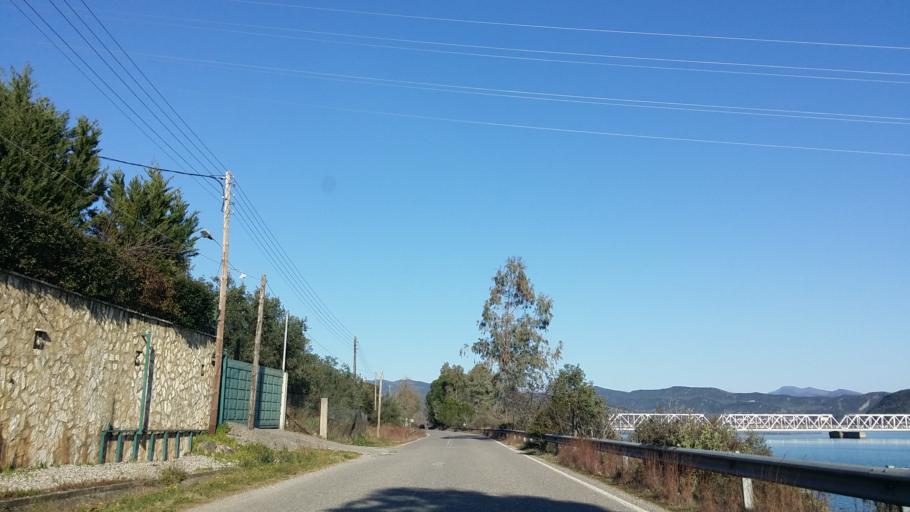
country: GR
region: West Greece
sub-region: Nomos Aitolias kai Akarnanias
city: Neapolis
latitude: 38.7098
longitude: 21.3369
